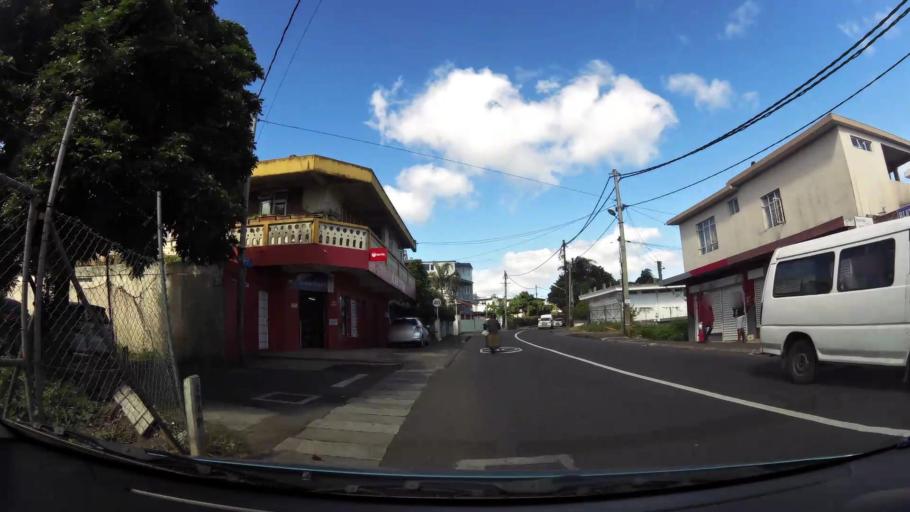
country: MU
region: Plaines Wilhems
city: Vacoas
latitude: -20.3105
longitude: 57.4897
